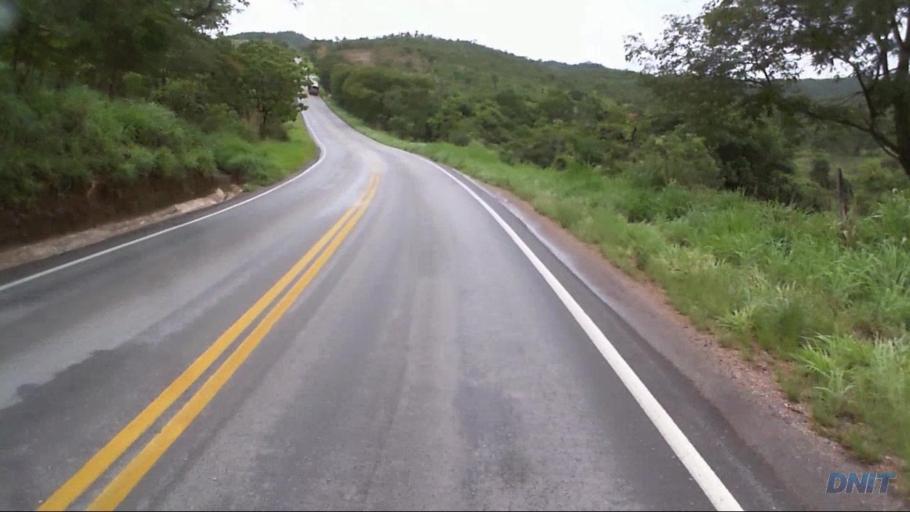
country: BR
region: Goias
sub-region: Padre Bernardo
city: Padre Bernardo
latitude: -15.4838
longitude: -48.2350
